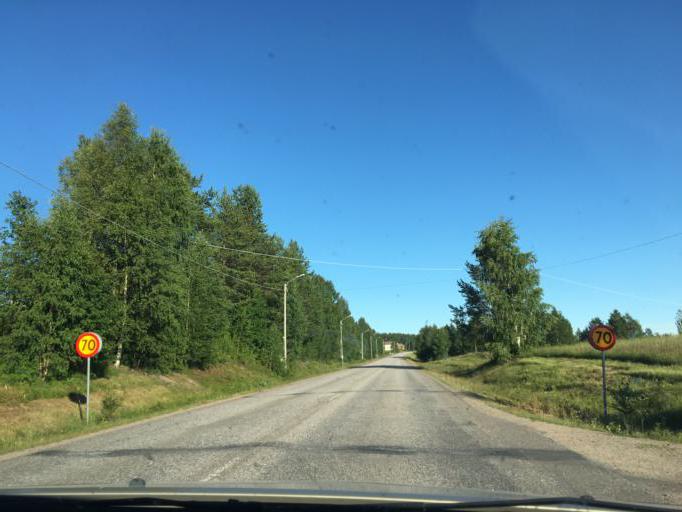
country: SE
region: Norrbotten
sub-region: Kalix Kommun
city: Rolfs
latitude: 65.9263
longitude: 22.9017
